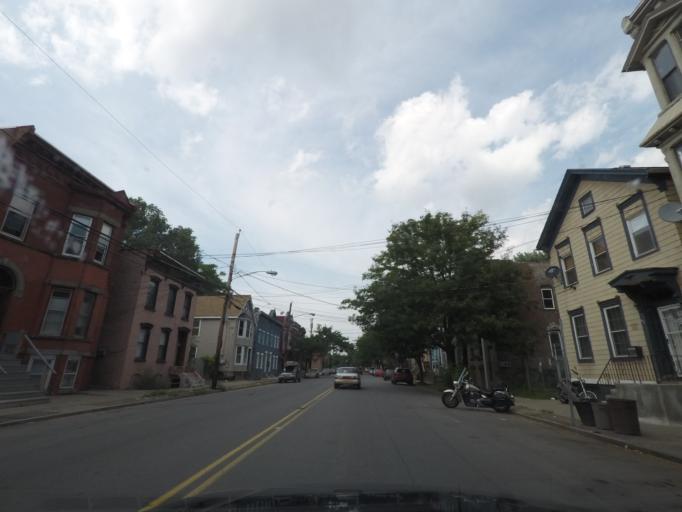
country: US
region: New York
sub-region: Albany County
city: Green Island
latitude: 42.7501
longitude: -73.6815
